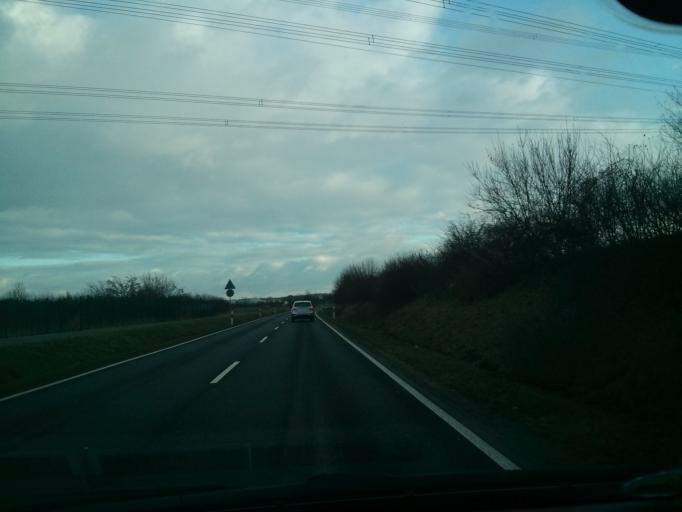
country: DE
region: North Rhine-Westphalia
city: Meckenheim
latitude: 50.6539
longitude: 7.0088
